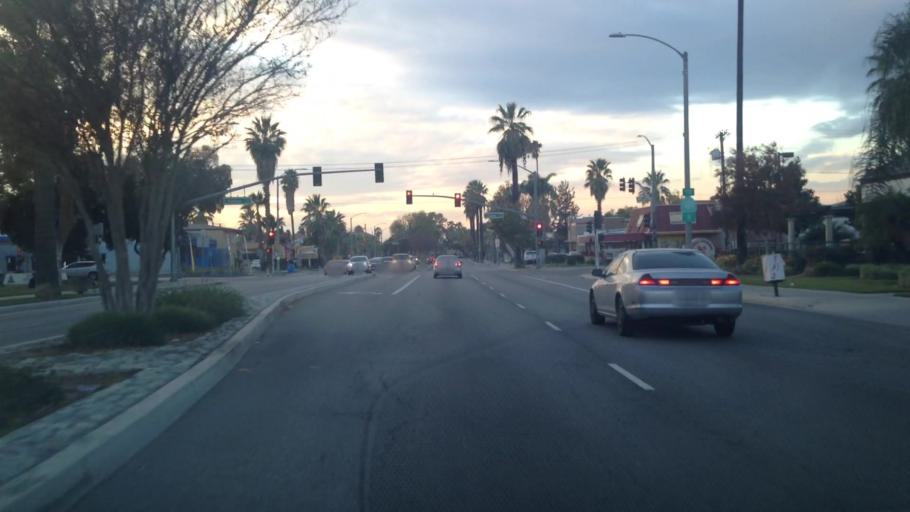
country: US
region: California
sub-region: Riverside County
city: Riverside
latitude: 33.9757
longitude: -117.3563
